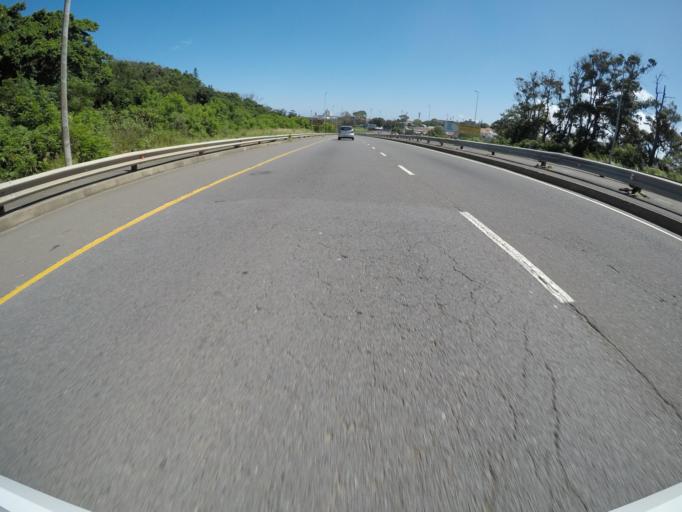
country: ZA
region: Eastern Cape
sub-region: Buffalo City Metropolitan Municipality
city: East London
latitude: -32.9995
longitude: 27.9145
